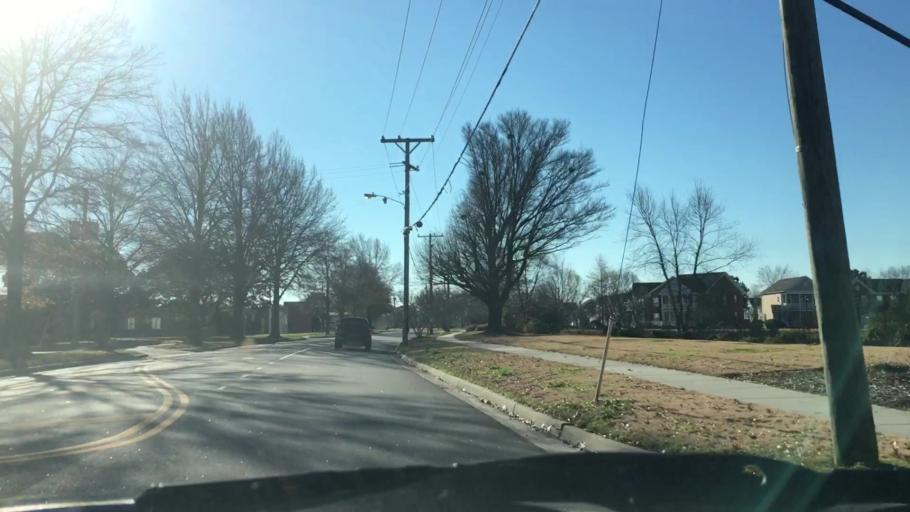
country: US
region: Virginia
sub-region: City of Norfolk
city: Norfolk
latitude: 36.8575
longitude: -76.2491
